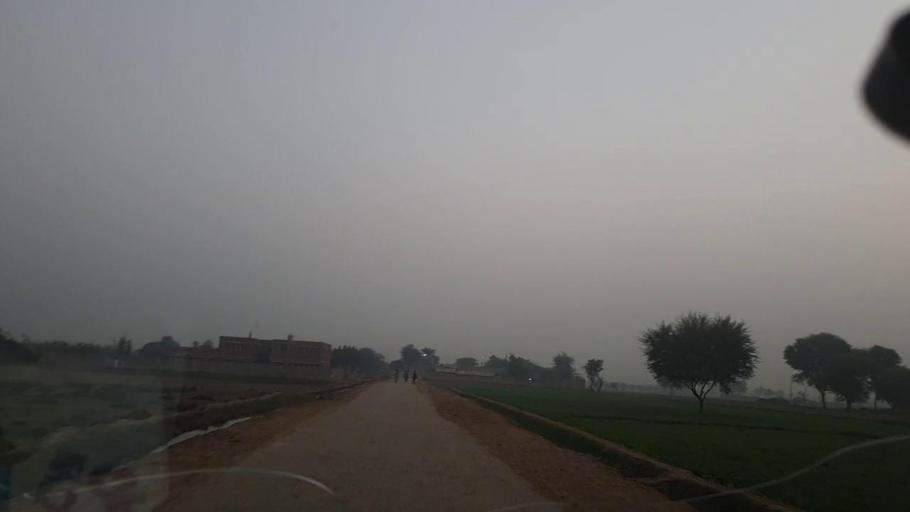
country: PK
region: Sindh
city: Hingorja
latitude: 27.2227
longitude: 68.4277
